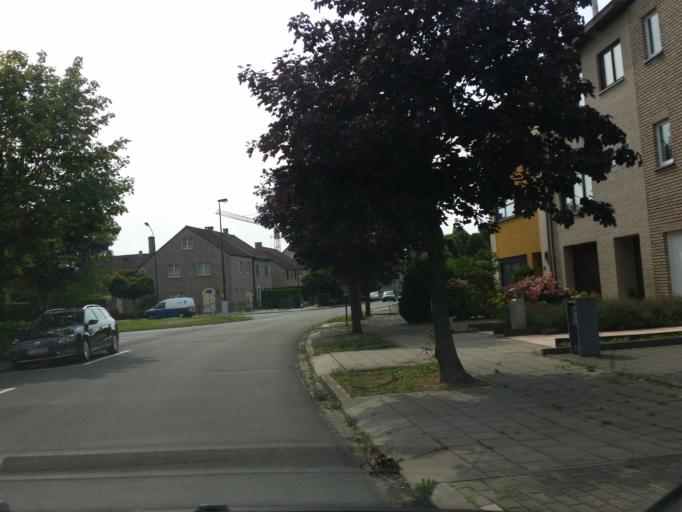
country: BE
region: Flanders
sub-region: Provincie Vlaams-Brabant
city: Vilvoorde
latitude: 50.9371
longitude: 4.4389
